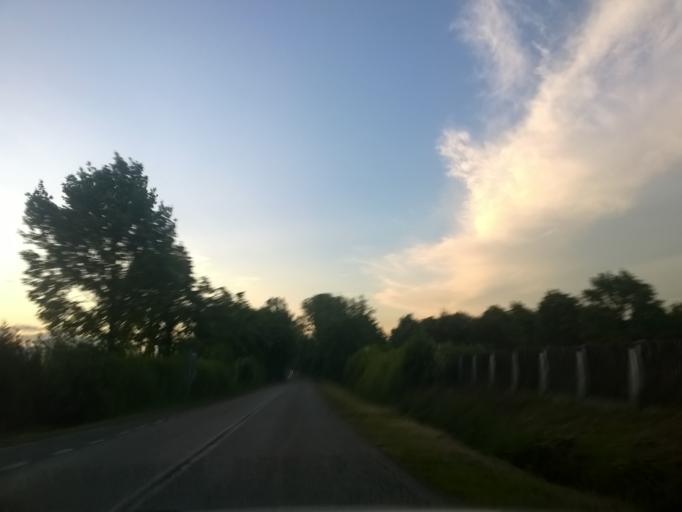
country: PL
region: Masovian Voivodeship
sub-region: Powiat piaseczynski
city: Baniocha
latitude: 52.0492
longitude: 21.1126
